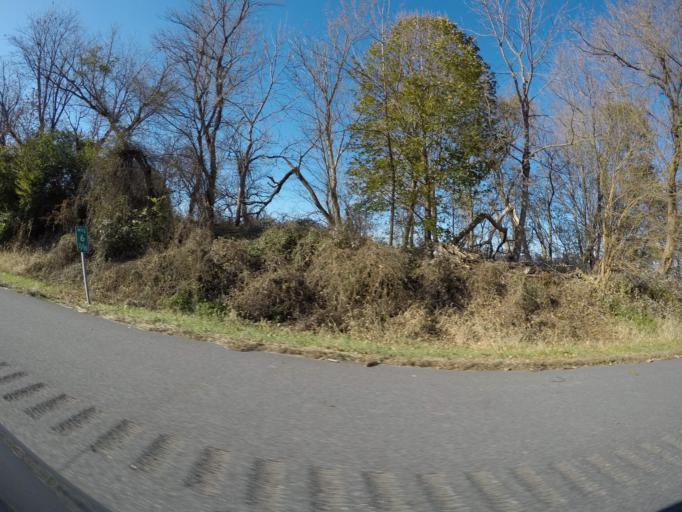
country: US
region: Pennsylvania
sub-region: Chester County
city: Oxford
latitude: 39.7993
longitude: -75.9817
